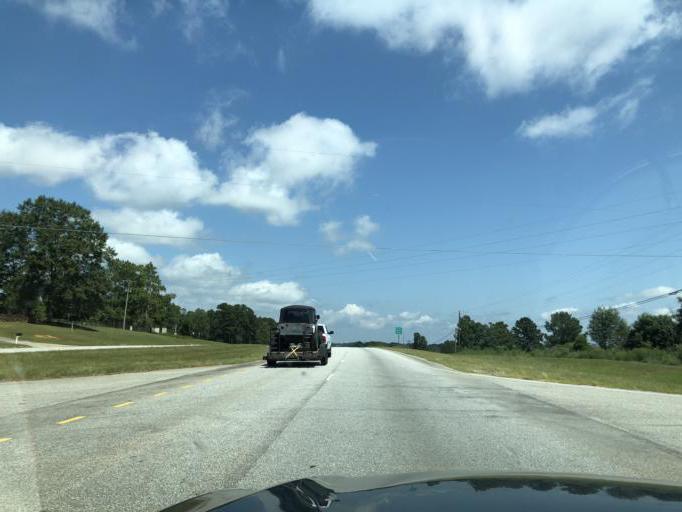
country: US
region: Alabama
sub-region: Barbour County
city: Eufaula
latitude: 31.7795
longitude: -85.1766
